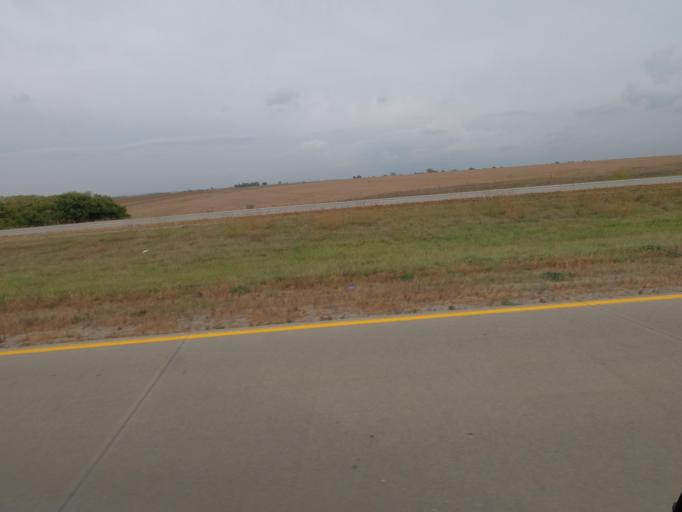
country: US
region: Iowa
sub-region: Mahaska County
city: Oskaloosa
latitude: 41.3434
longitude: -92.7440
